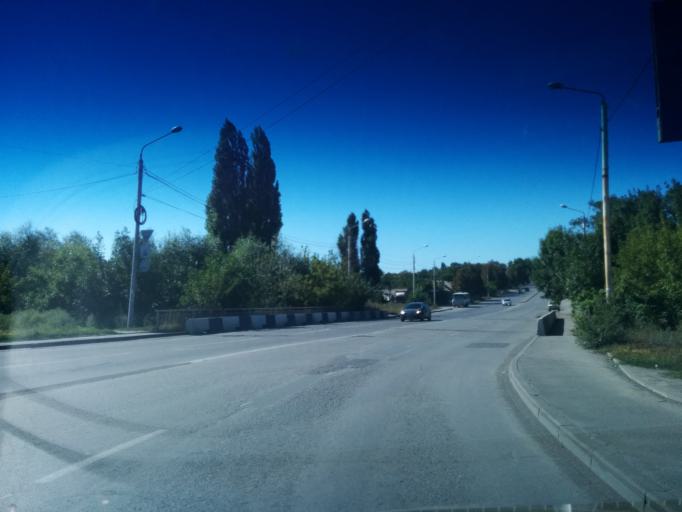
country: RU
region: Rostov
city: Shakhty
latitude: 47.6982
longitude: 40.2378
